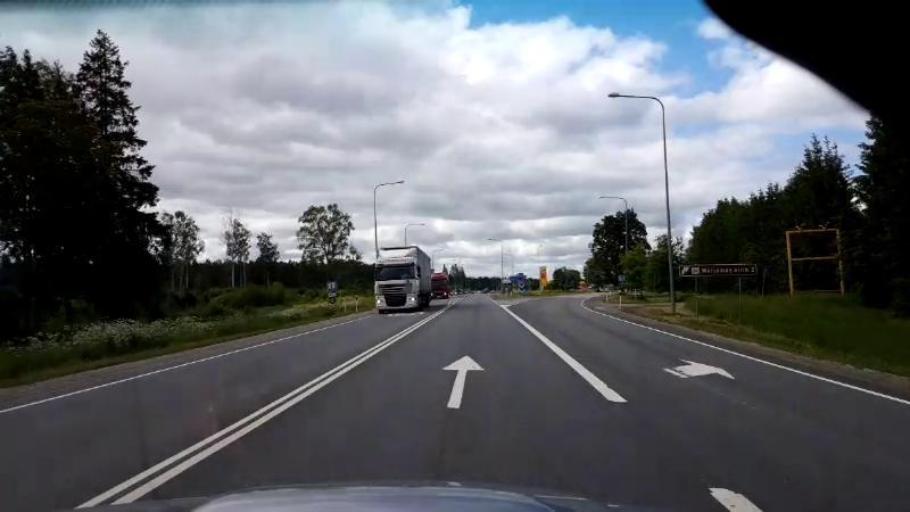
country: EE
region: Raplamaa
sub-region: Maerjamaa vald
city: Marjamaa
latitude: 58.9231
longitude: 24.4590
